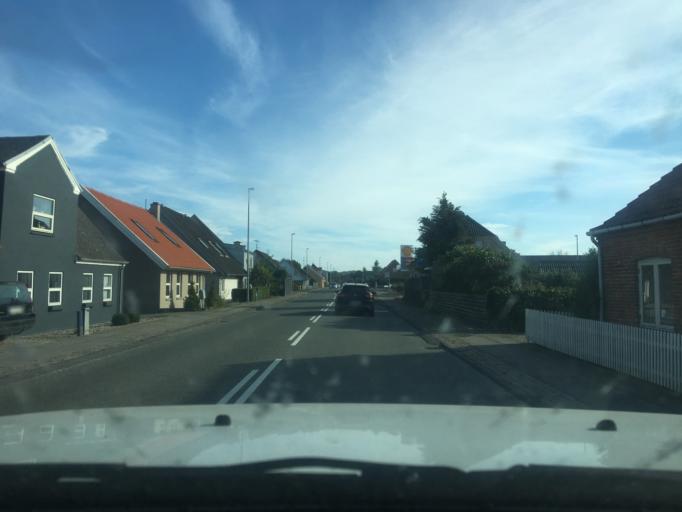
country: DK
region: Central Jutland
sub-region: Syddjurs Kommune
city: Hornslet
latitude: 56.3202
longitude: 10.3235
